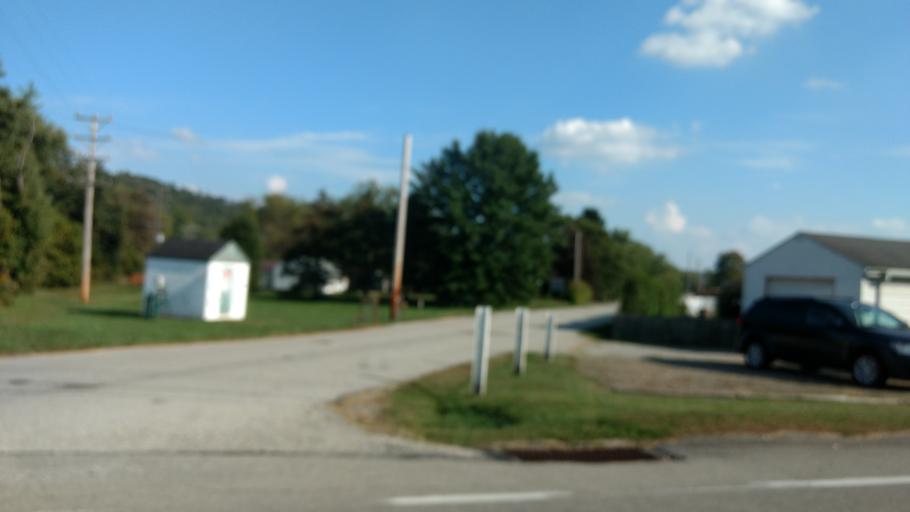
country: US
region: Pennsylvania
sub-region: Westmoreland County
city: Lynnwood-Pricedale
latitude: 40.1287
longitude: -79.8455
